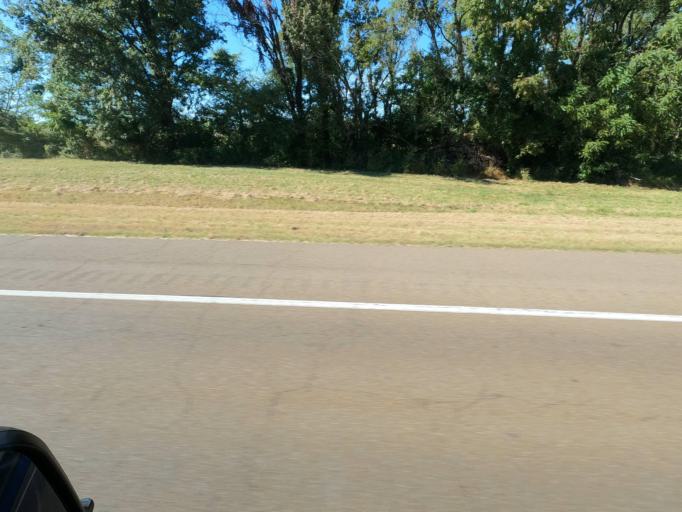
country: US
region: Tennessee
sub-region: Obion County
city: Union City
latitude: 36.4480
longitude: -89.0050
